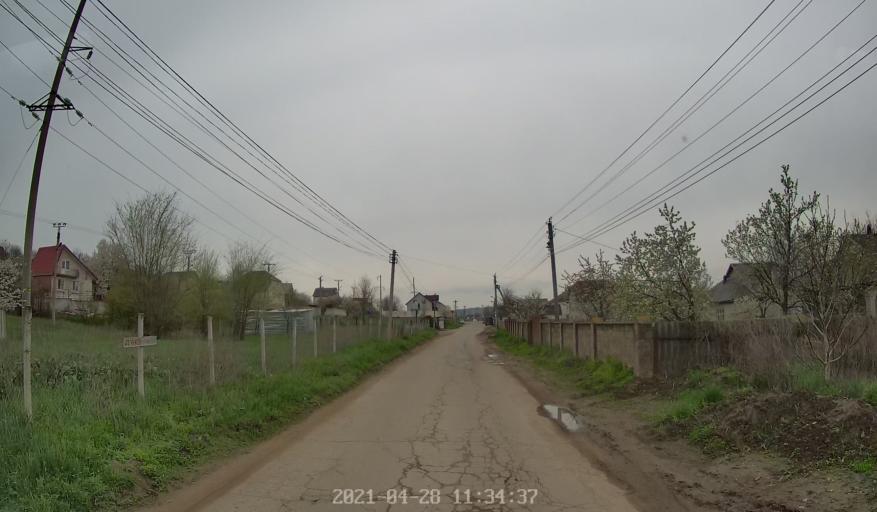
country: MD
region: Chisinau
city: Singera
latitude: 46.9541
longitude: 28.9421
